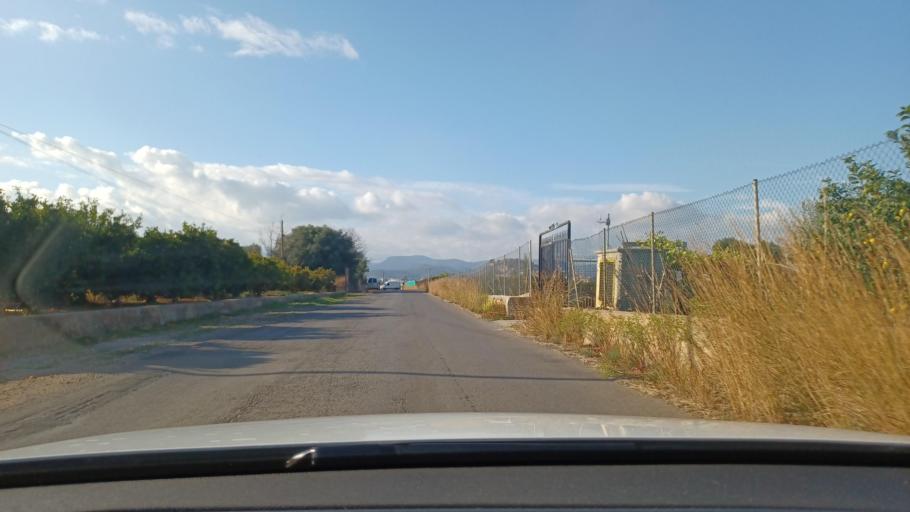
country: ES
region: Valencia
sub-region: Provincia de Castello
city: Onda
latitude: 39.9557
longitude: -0.2418
